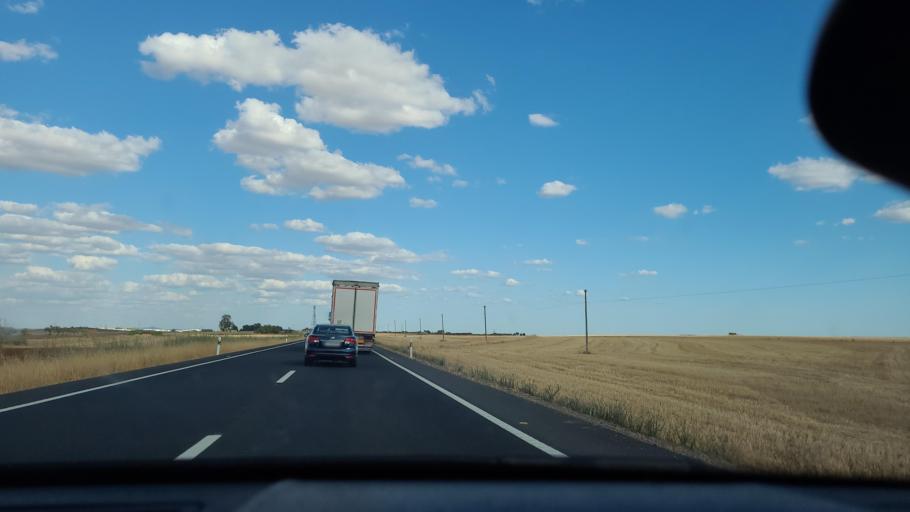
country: ES
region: Extremadura
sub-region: Provincia de Badajoz
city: Azuaga
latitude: 38.2629
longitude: -5.7345
